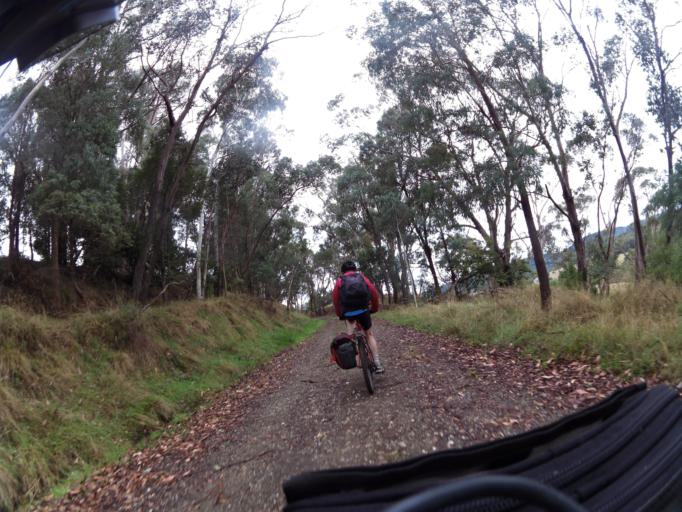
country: AU
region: New South Wales
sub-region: Greater Hume Shire
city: Holbrook
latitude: -36.1551
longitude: 147.4864
